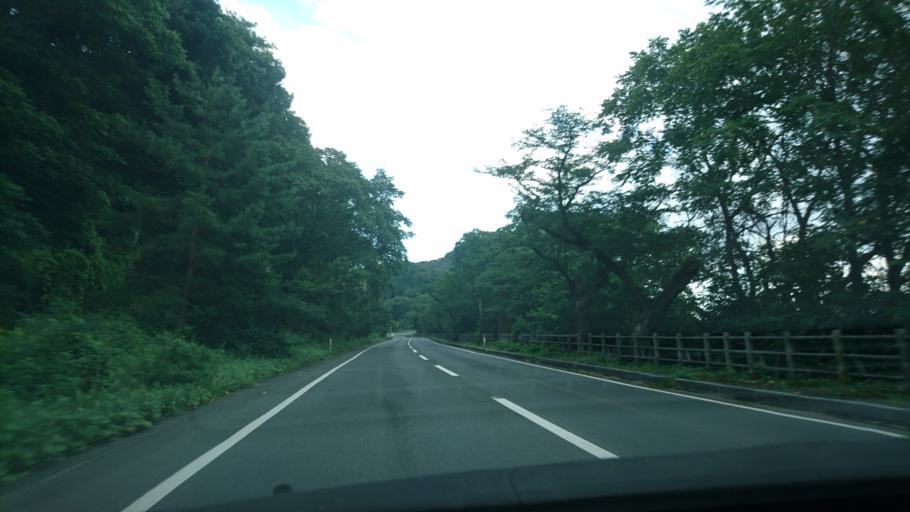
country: JP
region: Iwate
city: Kitakami
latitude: 39.2688
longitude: 141.1257
